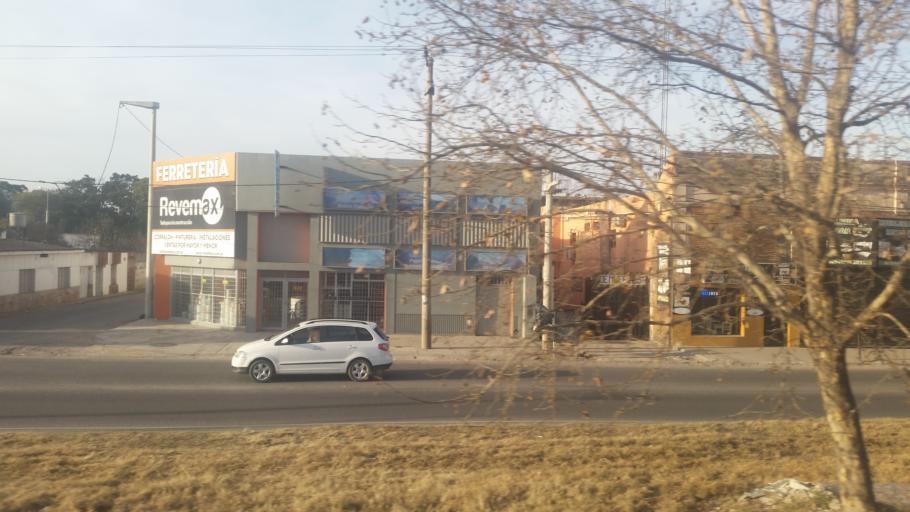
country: AR
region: Cordoba
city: Malvinas Argentinas
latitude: -31.4610
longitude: -64.1073
